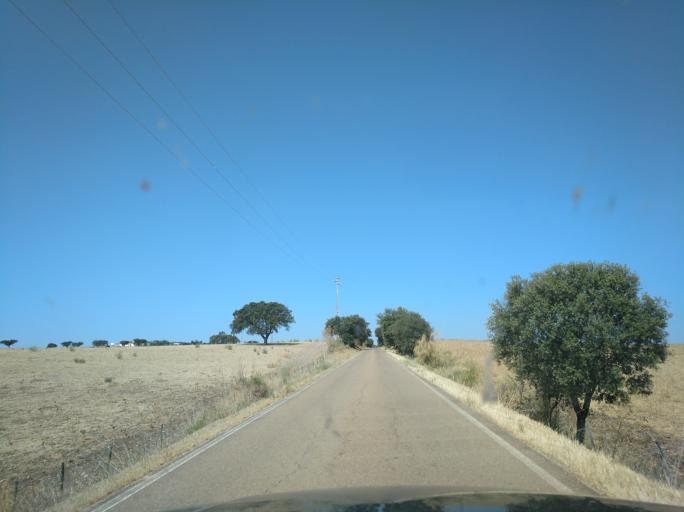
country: PT
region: Portalegre
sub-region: Campo Maior
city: Campo Maior
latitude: 39.0465
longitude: -7.0078
